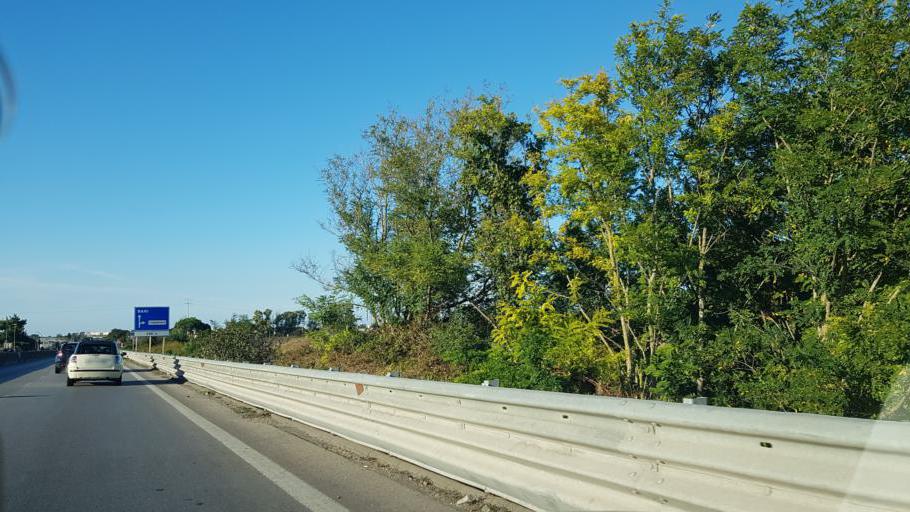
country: IT
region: Apulia
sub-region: Provincia di Brindisi
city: Brindisi
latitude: 40.6314
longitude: 17.9179
